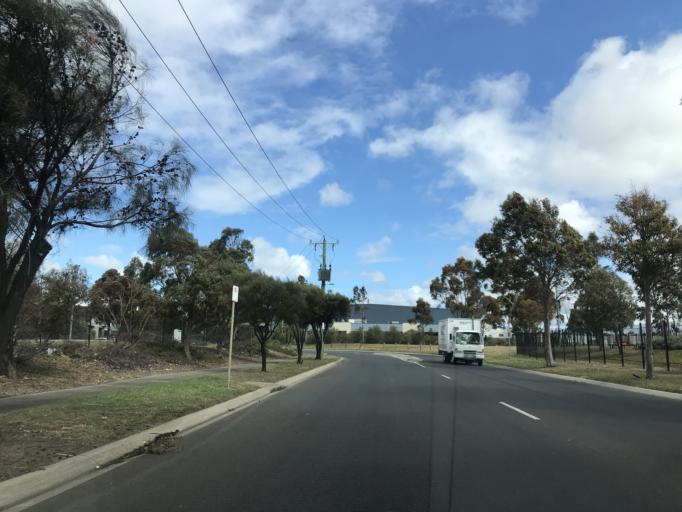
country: AU
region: Victoria
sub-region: Brimbank
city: Derrimut
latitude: -37.8041
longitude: 144.7793
